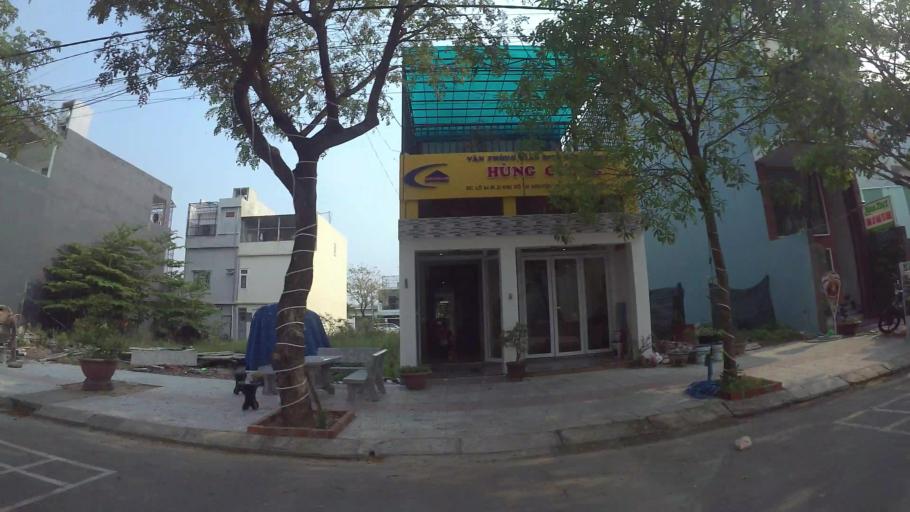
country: VN
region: Da Nang
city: Cam Le
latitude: 16.0038
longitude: 108.2259
